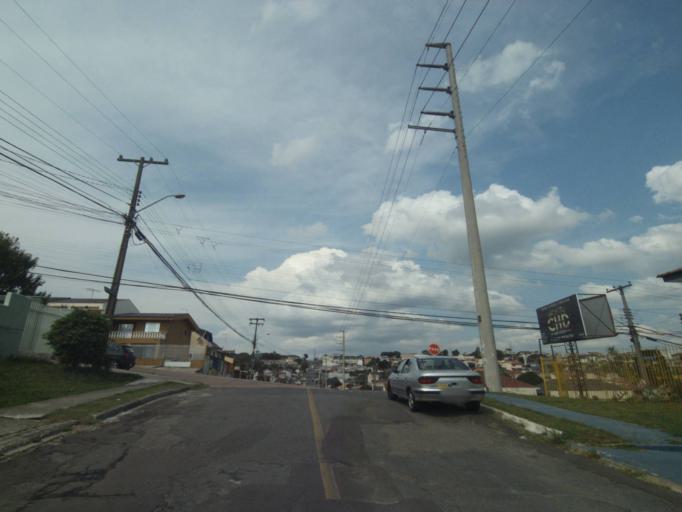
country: BR
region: Parana
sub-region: Pinhais
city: Pinhais
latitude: -25.4043
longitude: -49.2053
